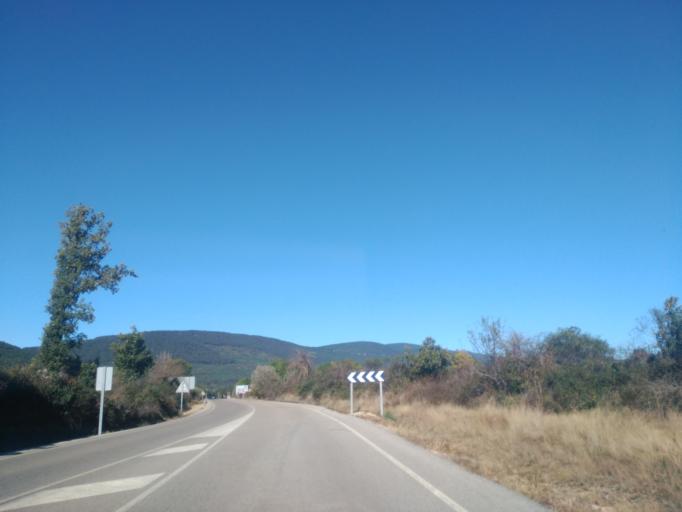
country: ES
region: Castille and Leon
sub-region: Provincia de Soria
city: Vinuesa
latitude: 41.9104
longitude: -2.7517
